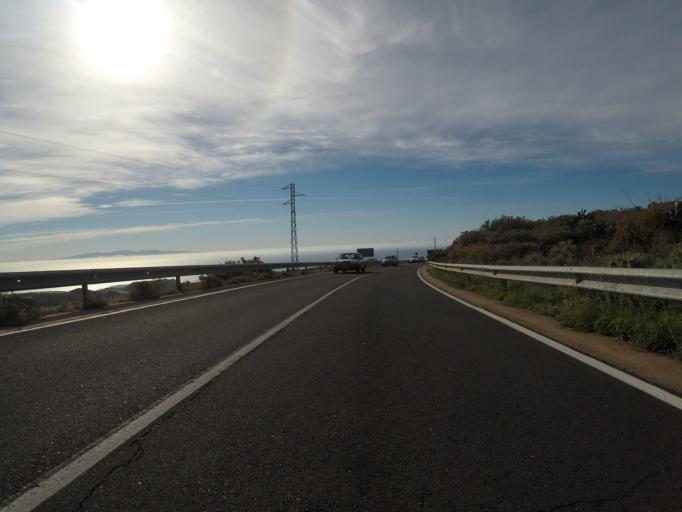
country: ES
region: Canary Islands
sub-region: Provincia de Santa Cruz de Tenerife
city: Lomo de Arico
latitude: 28.1657
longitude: -16.4994
